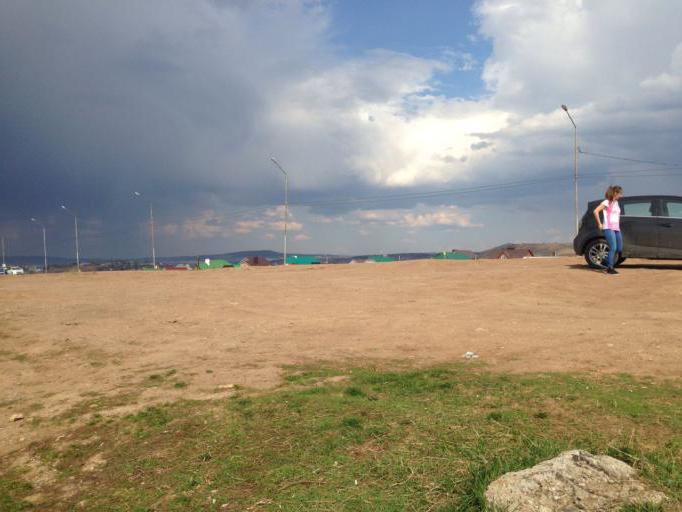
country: RU
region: Bashkortostan
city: Oktyabr'skiy
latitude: 54.4530
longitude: 53.4452
